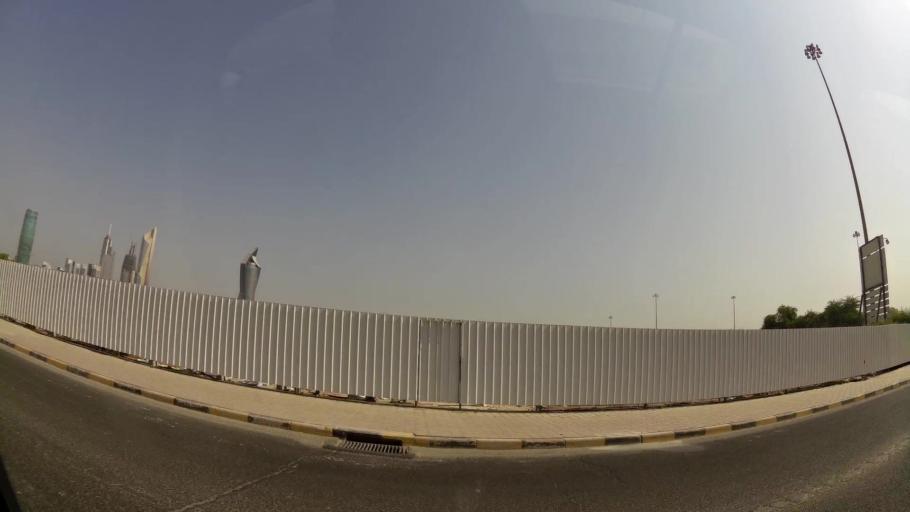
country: KW
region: Al Asimah
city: Kuwait City
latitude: 29.3623
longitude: 47.9867
